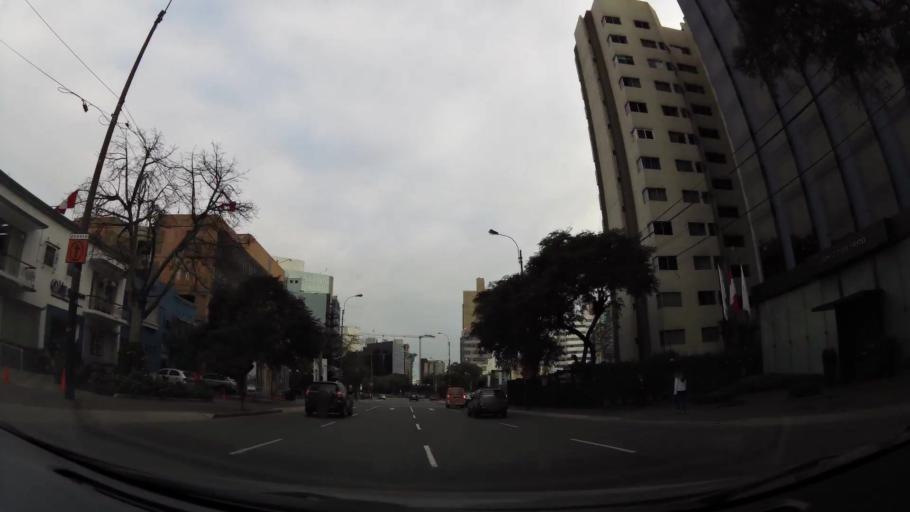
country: PE
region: Lima
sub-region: Lima
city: San Isidro
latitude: -12.1040
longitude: -77.0389
